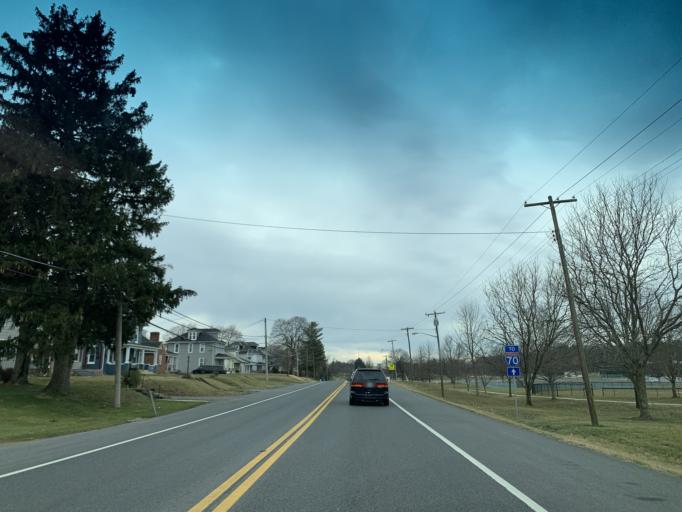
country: US
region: Maryland
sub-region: Washington County
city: Hagerstown
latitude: 39.6222
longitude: -77.7288
